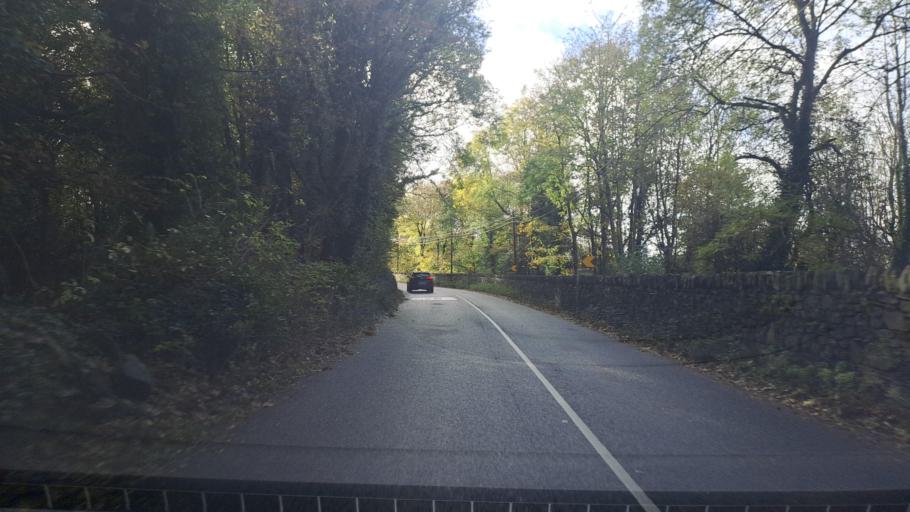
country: IE
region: Ulster
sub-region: County Monaghan
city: Monaghan
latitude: 54.2179
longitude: -6.9831
